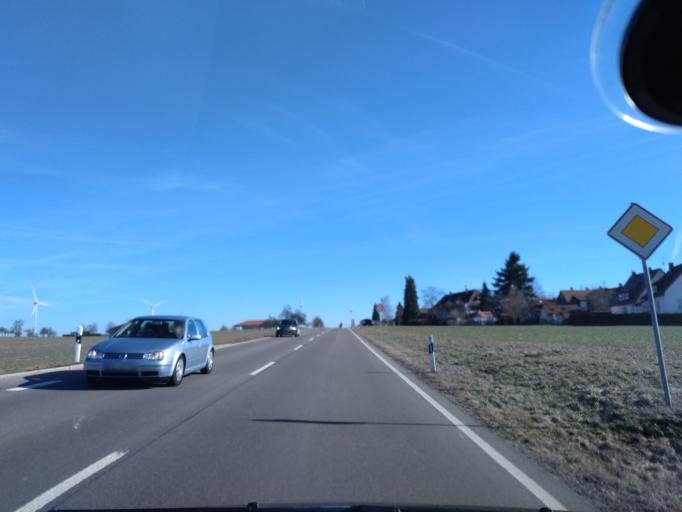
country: DE
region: Baden-Wuerttemberg
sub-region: Regierungsbezirk Stuttgart
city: Mainhardt
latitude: 49.0863
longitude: 9.6085
